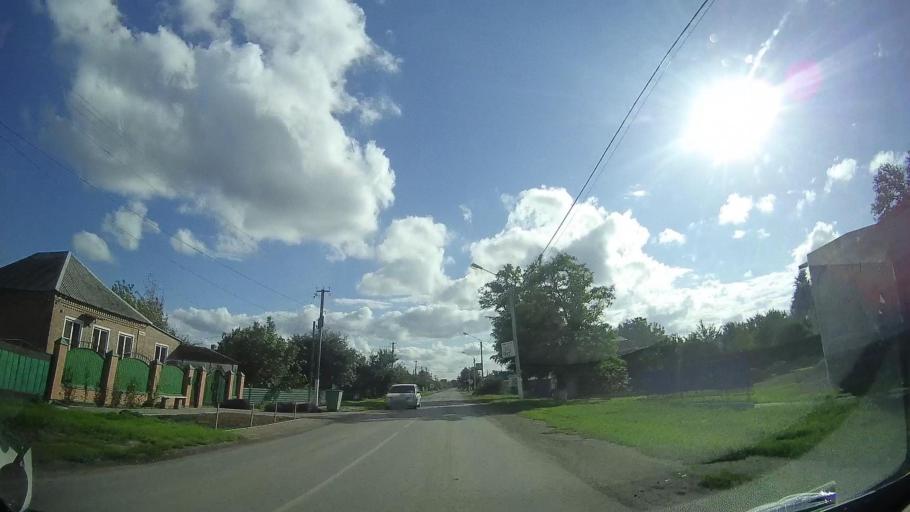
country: RU
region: Rostov
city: Tselina
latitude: 46.5366
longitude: 41.0340
